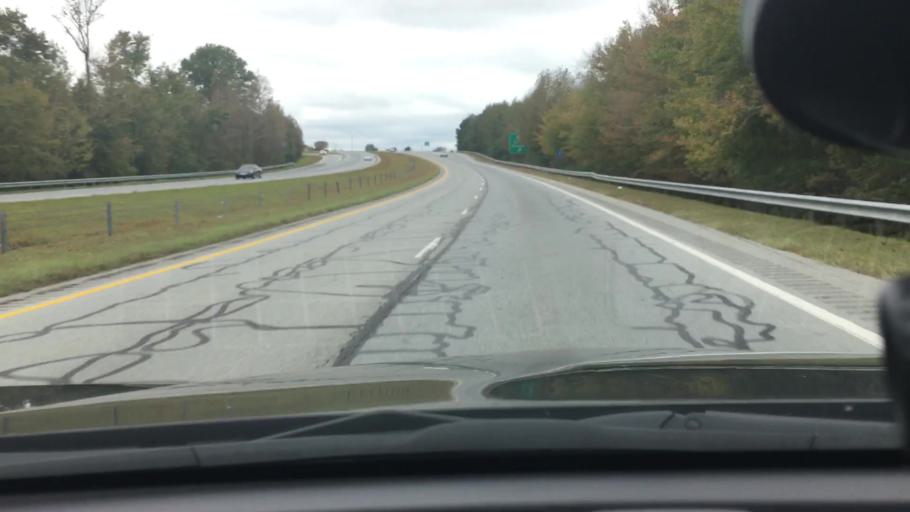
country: US
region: North Carolina
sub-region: Pitt County
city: Farmville
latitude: 35.6205
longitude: -77.5993
